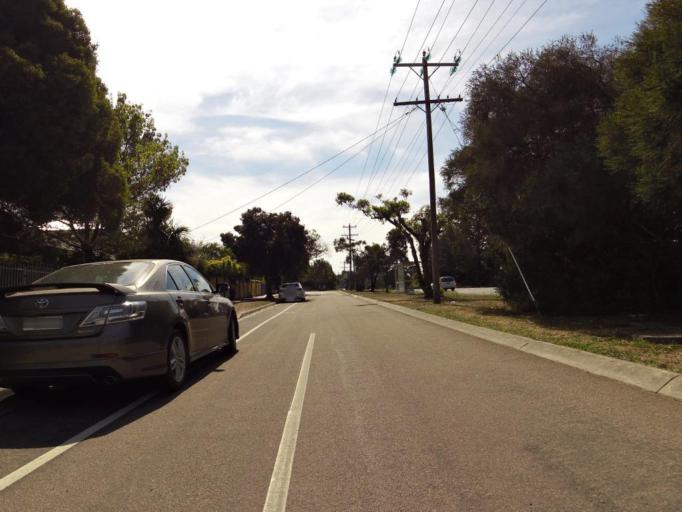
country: AU
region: Victoria
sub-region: Mornington Peninsula
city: Tyabb
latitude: -38.2321
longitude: 145.1831
